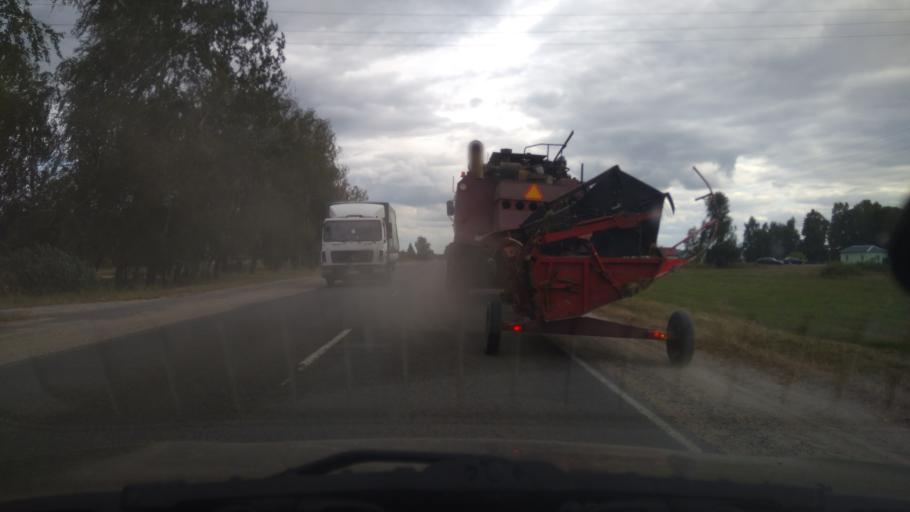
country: BY
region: Brest
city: Byelaazyorsk
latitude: 52.4913
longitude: 25.1925
